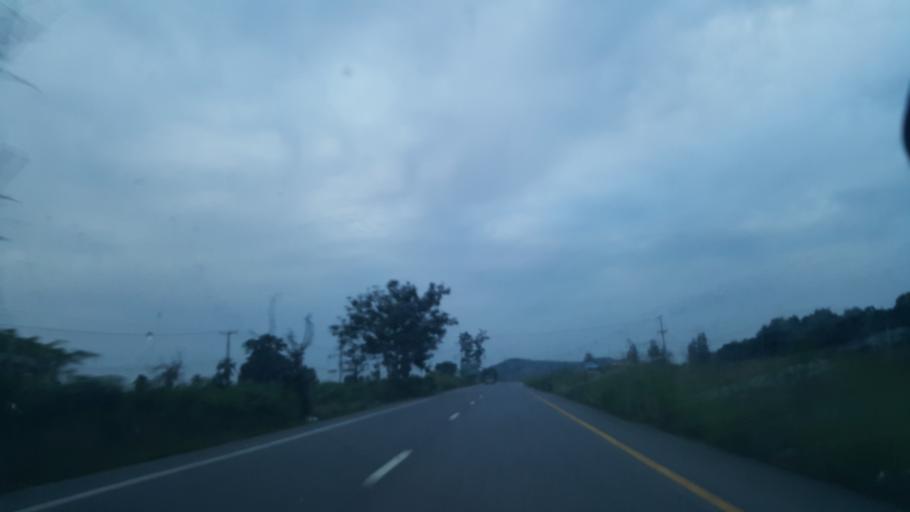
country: TH
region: Rayong
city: Ban Chang
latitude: 12.8183
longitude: 100.9976
